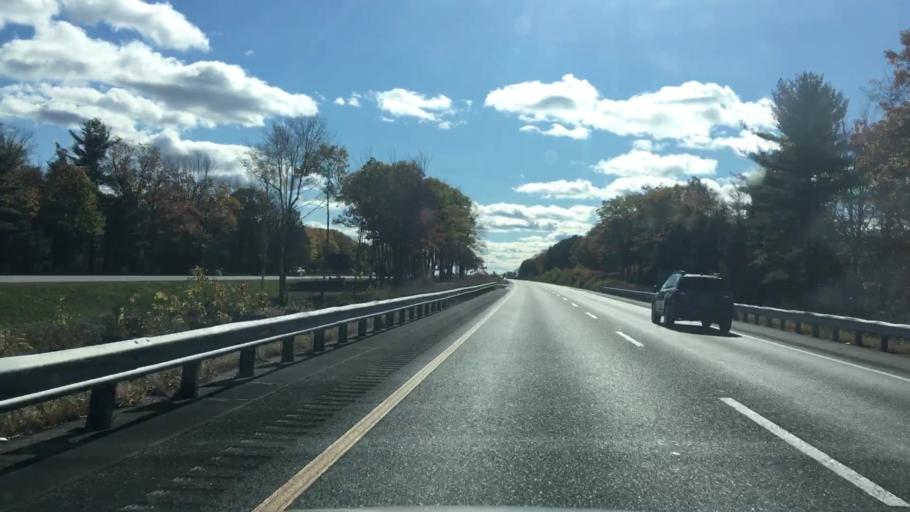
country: US
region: Maine
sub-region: Kennebec County
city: Waterville
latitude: 44.5546
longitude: -69.6761
